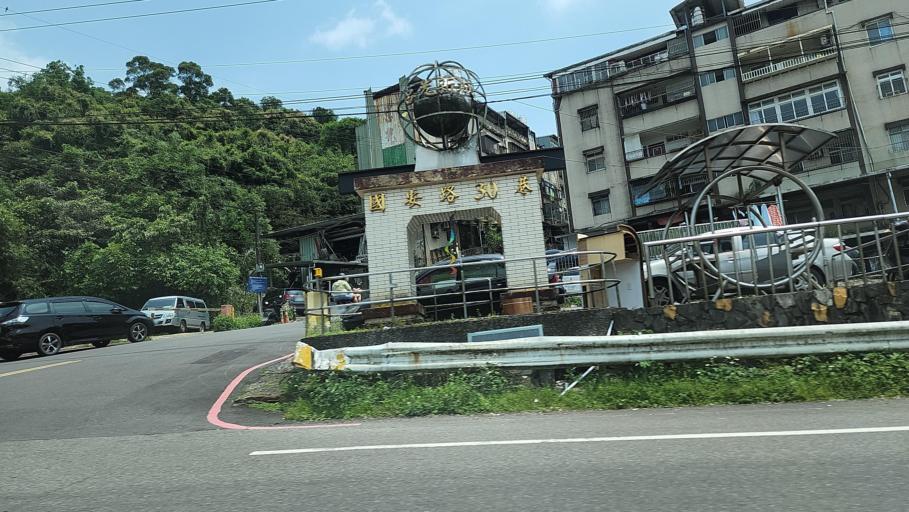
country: TW
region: Taiwan
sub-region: Keelung
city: Keelung
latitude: 25.1119
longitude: 121.7346
